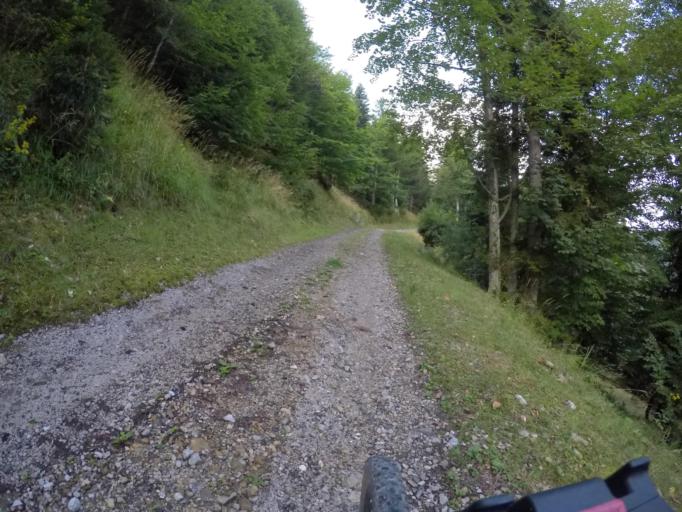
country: IT
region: Friuli Venezia Giulia
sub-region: Provincia di Udine
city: Paularo
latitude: 46.4984
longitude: 13.1814
